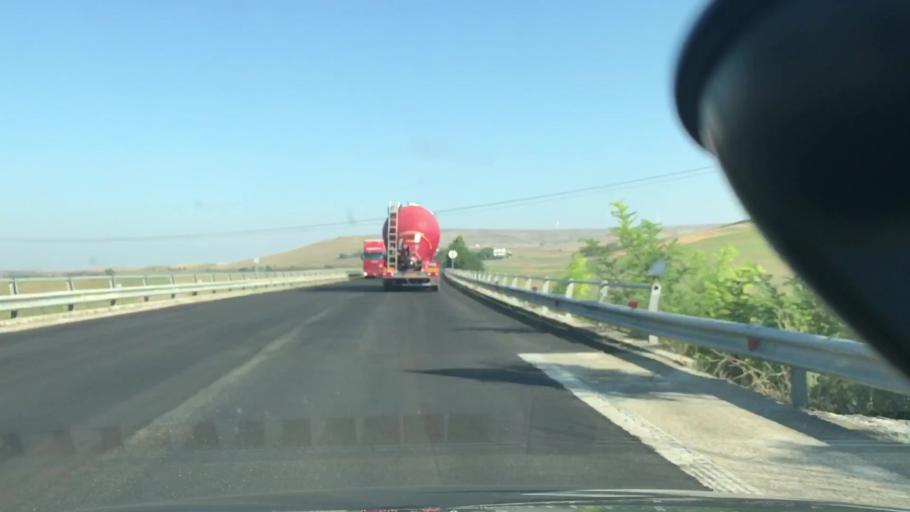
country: IT
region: Basilicate
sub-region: Provincia di Matera
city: Irsina
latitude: 40.7977
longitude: 16.2751
